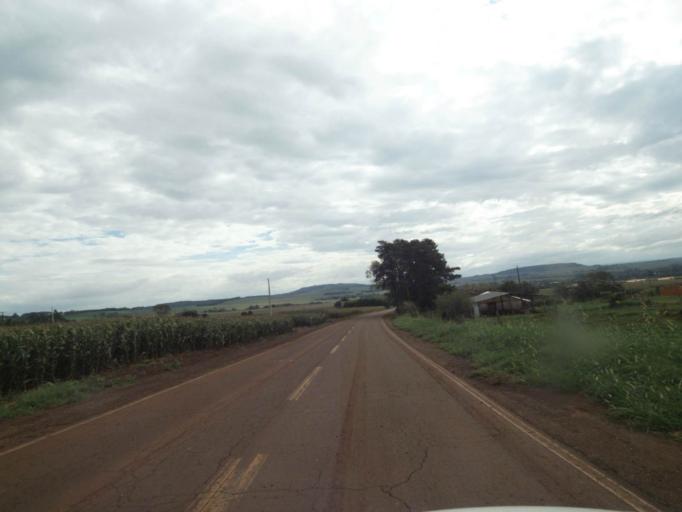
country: BR
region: Parana
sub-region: Marechal Candido Rondon
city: Marechal Candido Rondon
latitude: -24.7928
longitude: -54.2268
